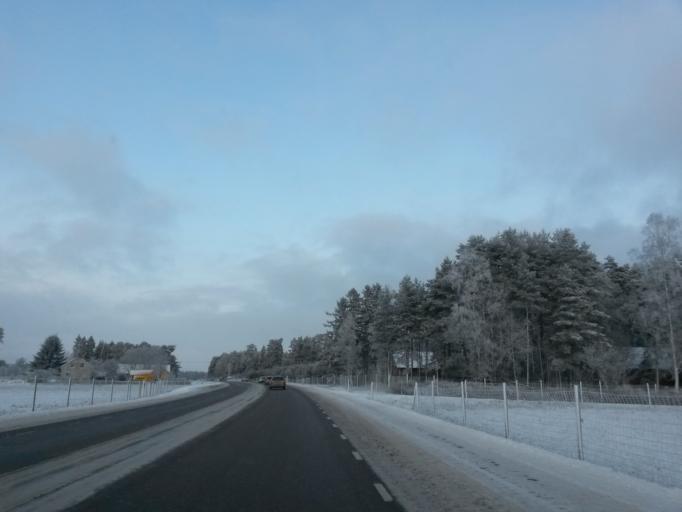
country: SE
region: Vaestra Goetaland
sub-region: Vara Kommun
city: Vara
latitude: 58.1919
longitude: 12.8999
